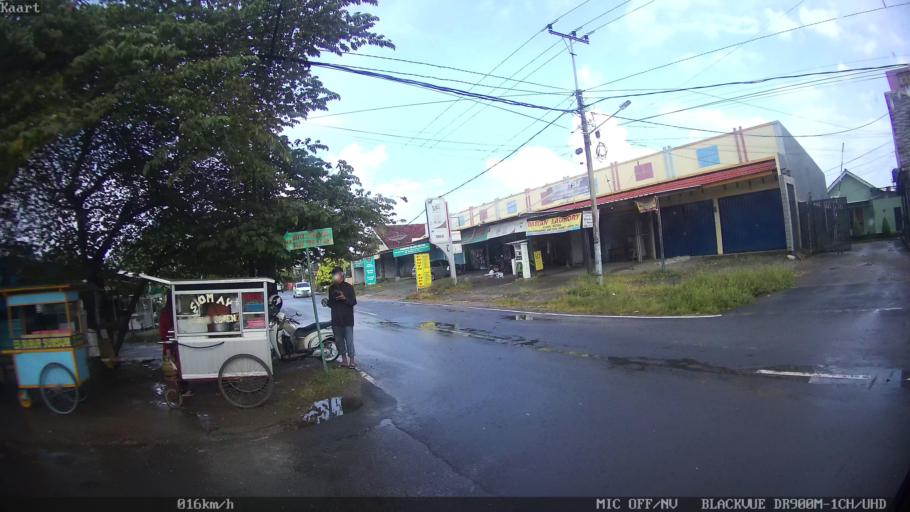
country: ID
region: Lampung
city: Kedaton
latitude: -5.3907
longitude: 105.3054
